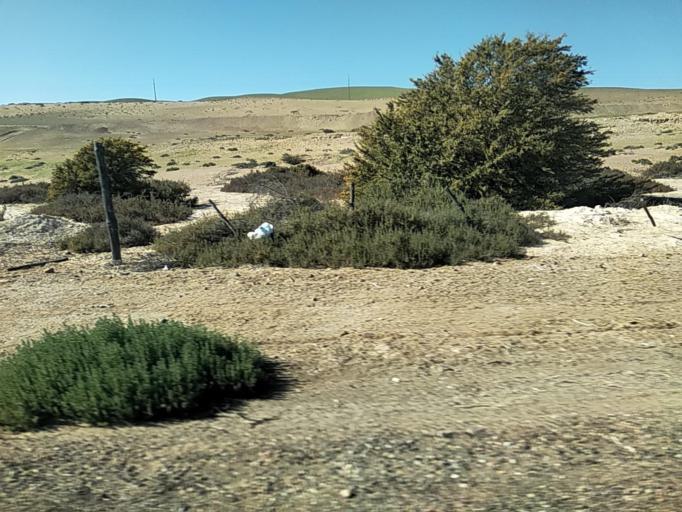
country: CL
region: Atacama
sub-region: Provincia de Copiapo
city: Copiapo
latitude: -27.3431
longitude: -70.7545
